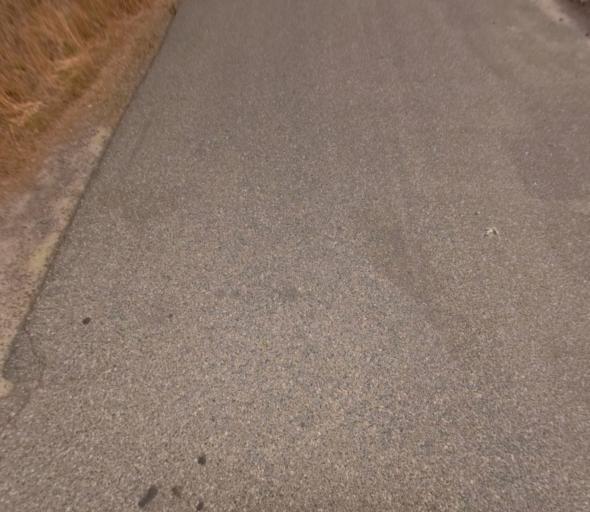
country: US
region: California
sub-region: Madera County
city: Coarsegold
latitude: 37.2183
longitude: -119.7088
